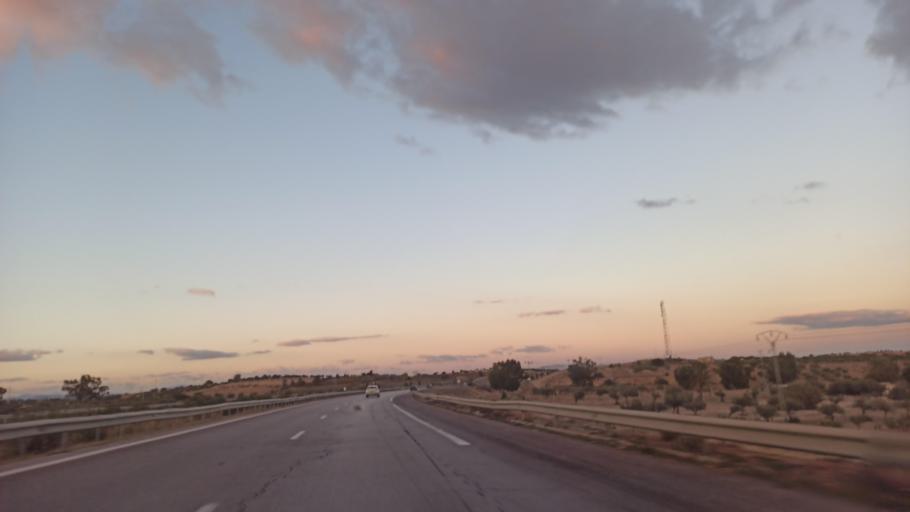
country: TN
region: Susah
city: Harqalah
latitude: 36.2342
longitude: 10.4136
